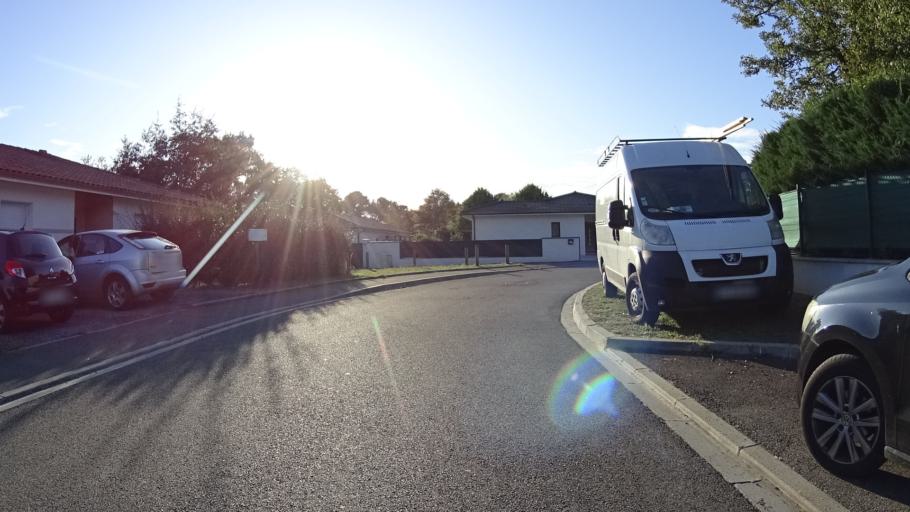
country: FR
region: Aquitaine
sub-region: Departement des Landes
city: Saint-Paul-les-Dax
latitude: 43.7389
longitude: -1.0463
